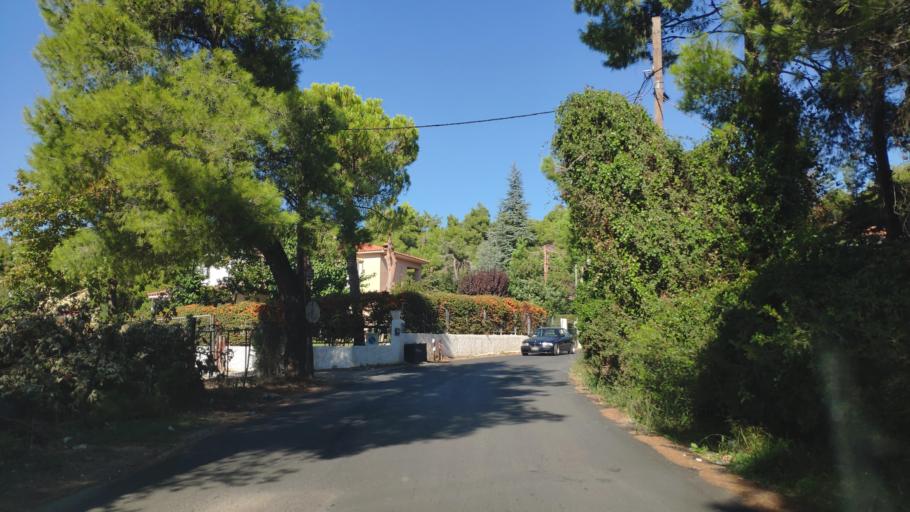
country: GR
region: Attica
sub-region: Nomarchia Anatolikis Attikis
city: Drosia
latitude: 38.1240
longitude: 23.8713
